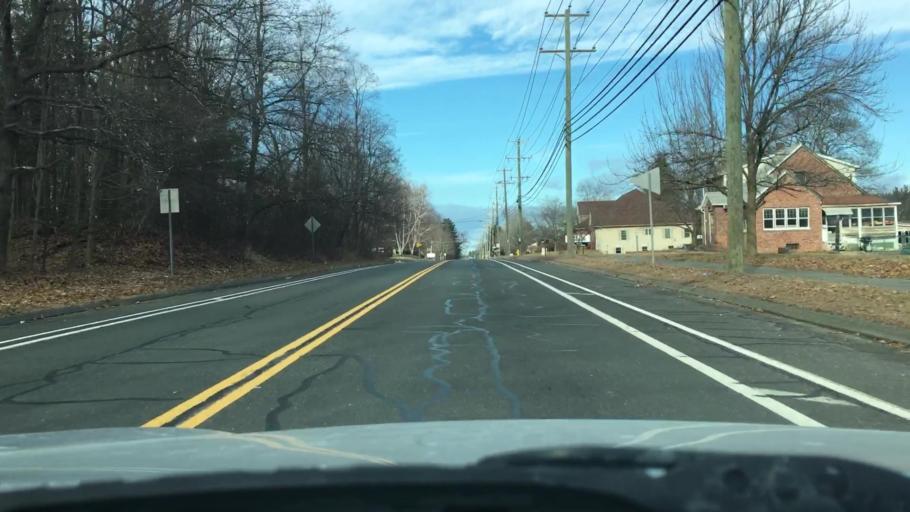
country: US
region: Massachusetts
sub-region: Hampden County
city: Agawam
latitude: 42.0504
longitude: -72.6345
